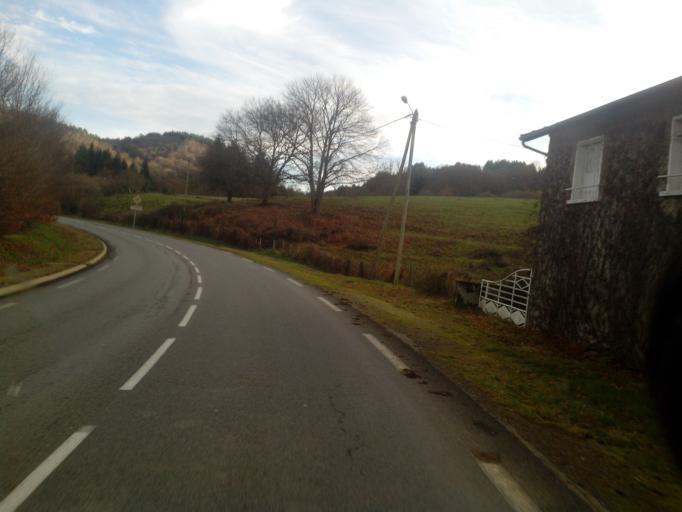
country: FR
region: Limousin
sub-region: Departement de la Haute-Vienne
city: Eymoutiers
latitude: 45.6852
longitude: 1.7928
